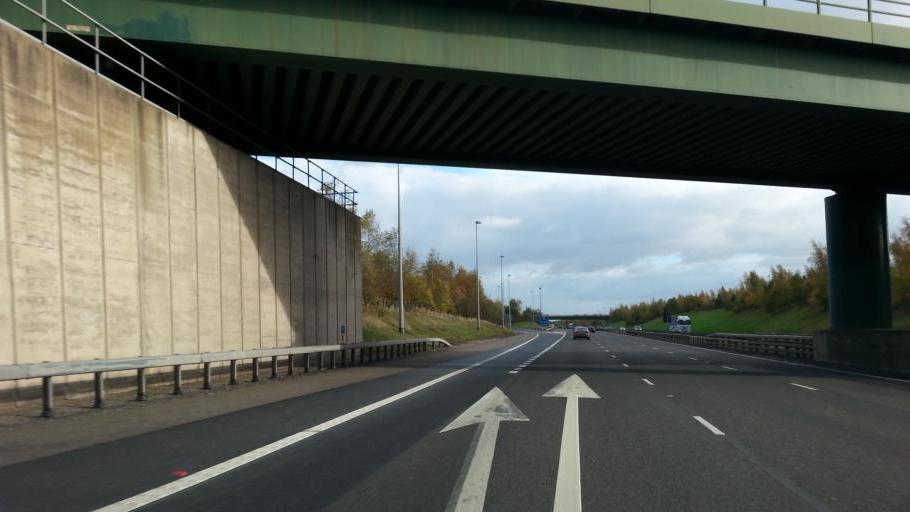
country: GB
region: England
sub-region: Staffordshire
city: Shenstone
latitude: 52.6501
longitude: -1.8411
